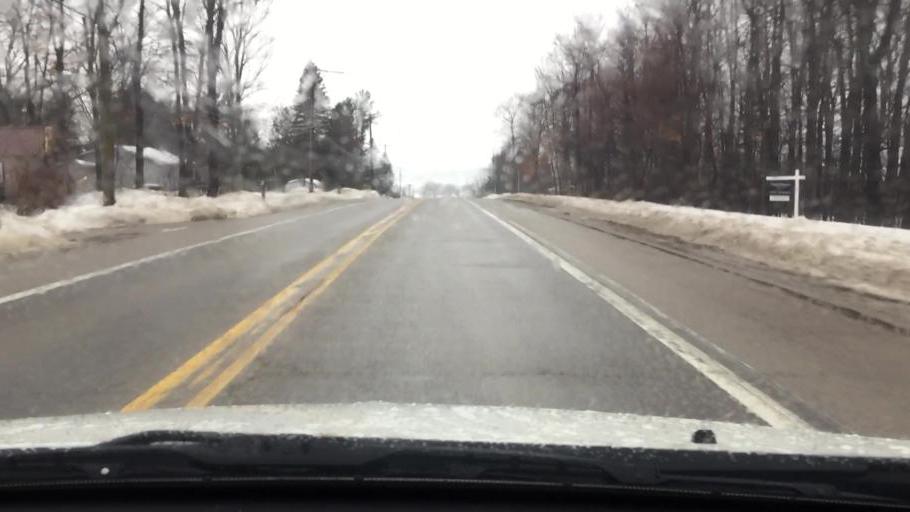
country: US
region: Michigan
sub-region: Charlevoix County
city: East Jordan
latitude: 45.1474
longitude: -85.1398
